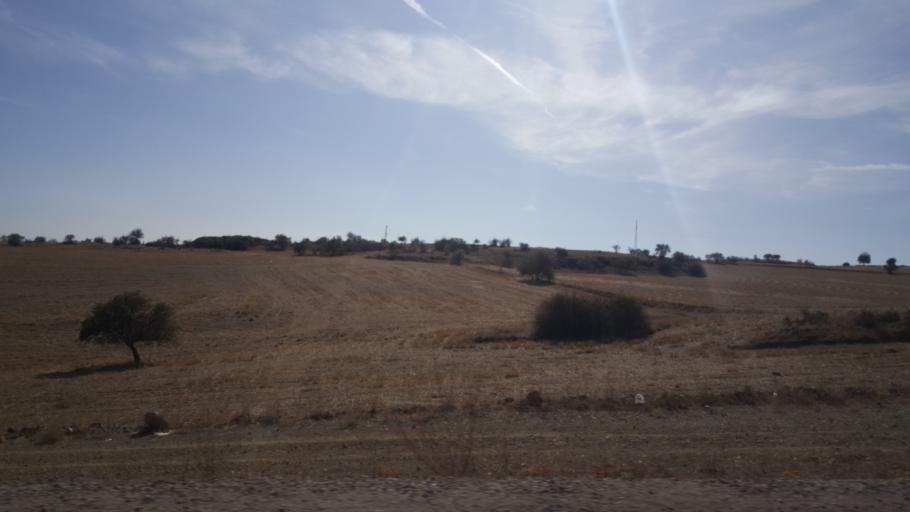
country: TR
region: Ankara
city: Haymana
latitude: 39.4287
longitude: 32.5503
